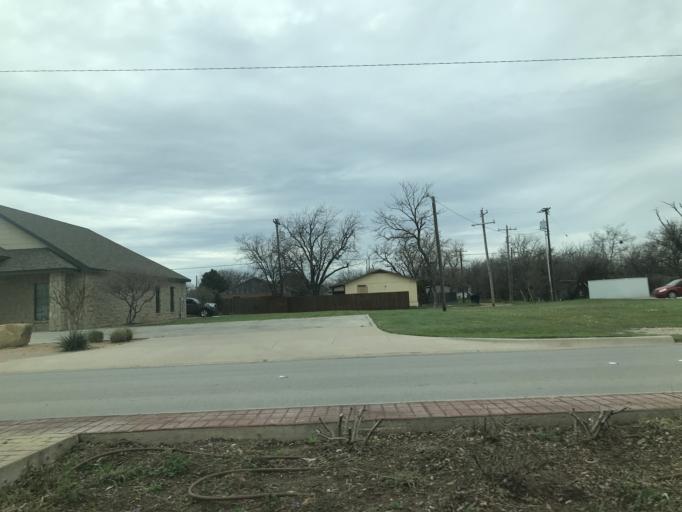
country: US
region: Texas
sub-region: Taylor County
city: Abilene
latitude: 32.4664
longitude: -99.7314
